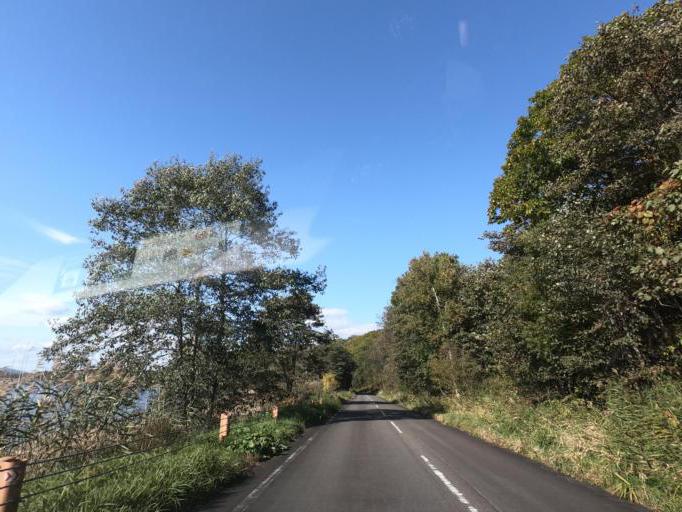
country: JP
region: Hokkaido
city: Obihiro
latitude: 42.6132
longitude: 143.5443
